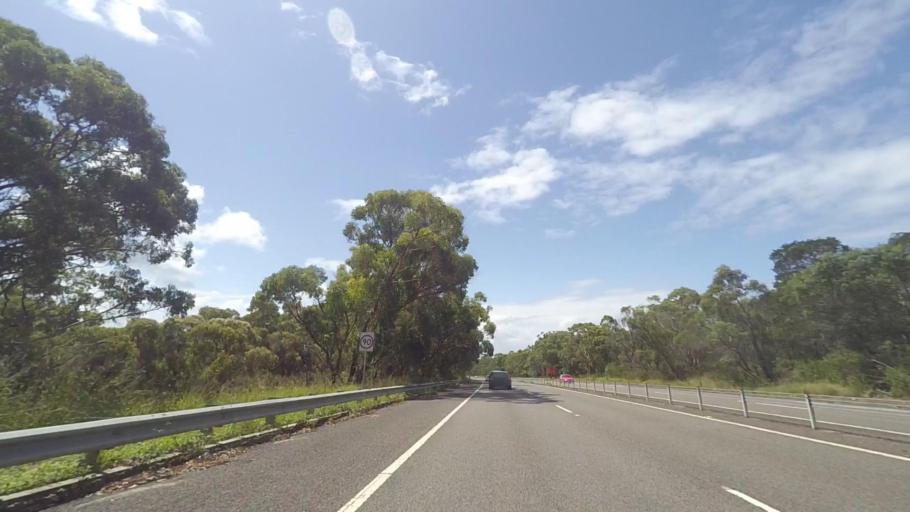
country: AU
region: New South Wales
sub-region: Wyong Shire
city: Kingfisher Shores
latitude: -33.1495
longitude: 151.6133
